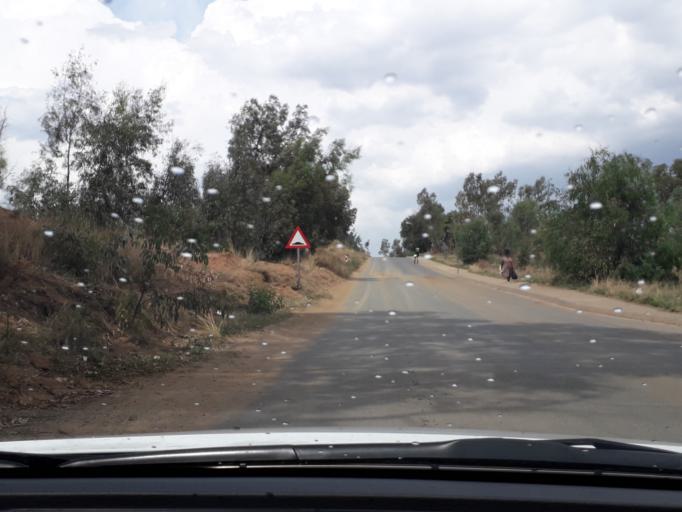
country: ZA
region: Gauteng
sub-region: West Rand District Municipality
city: Muldersdriseloop
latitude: -26.0038
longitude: 27.8539
